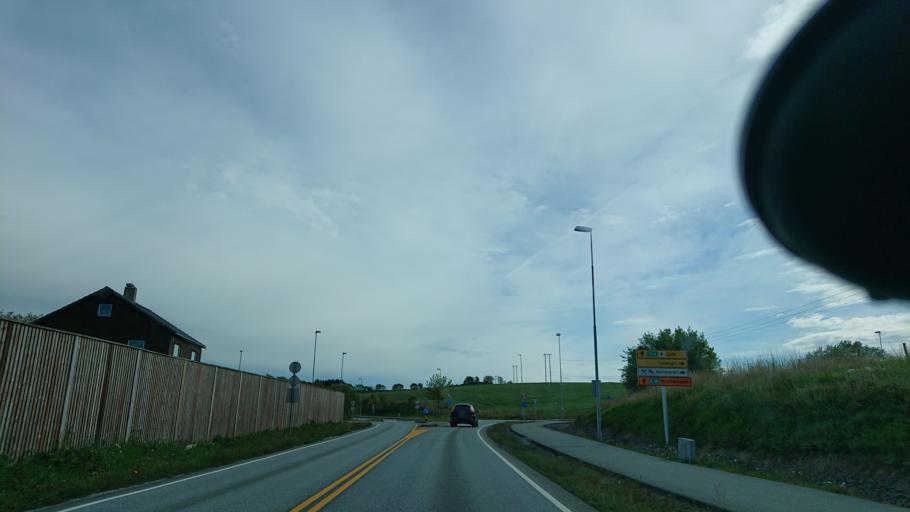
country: NO
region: Rogaland
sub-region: Sola
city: Tananger
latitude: 58.9451
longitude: 5.5989
